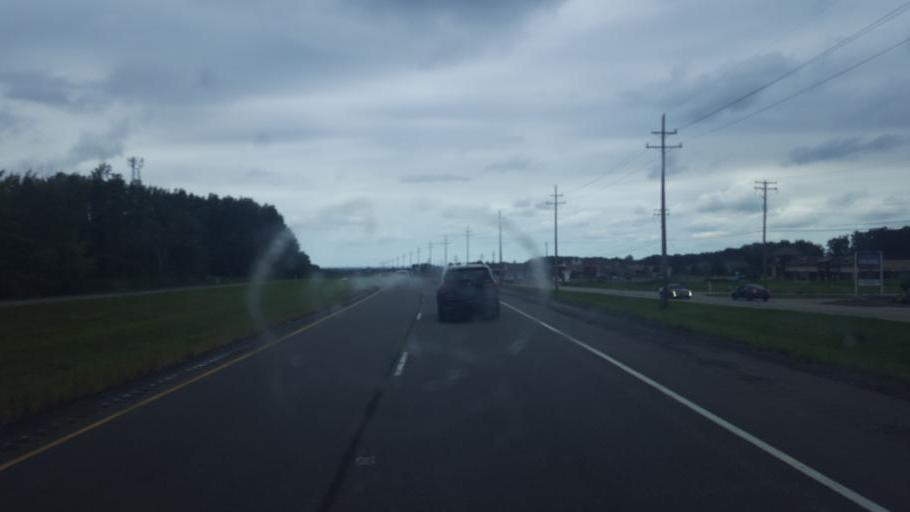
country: US
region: Ohio
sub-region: Lake County
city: Painesville
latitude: 41.6606
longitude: -81.2407
